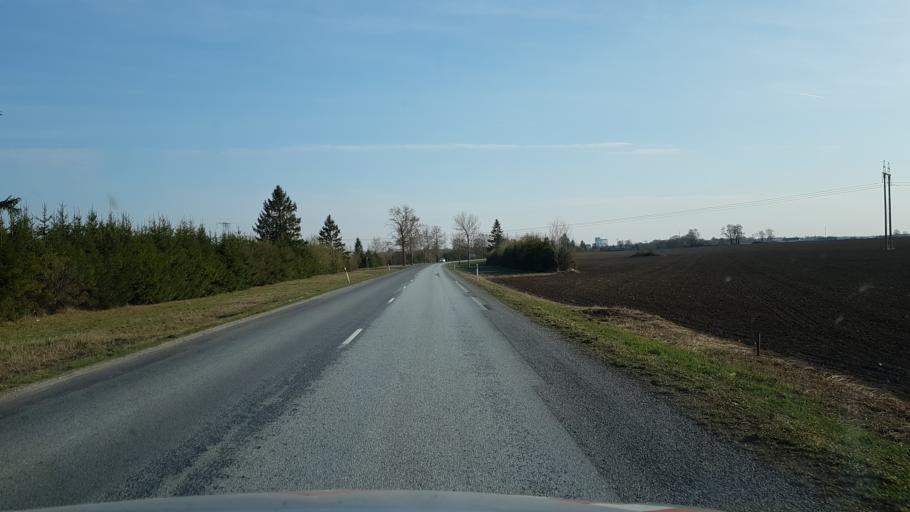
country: EE
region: Laeaene-Virumaa
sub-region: Someru vald
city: Someru
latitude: 59.3811
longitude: 26.3923
